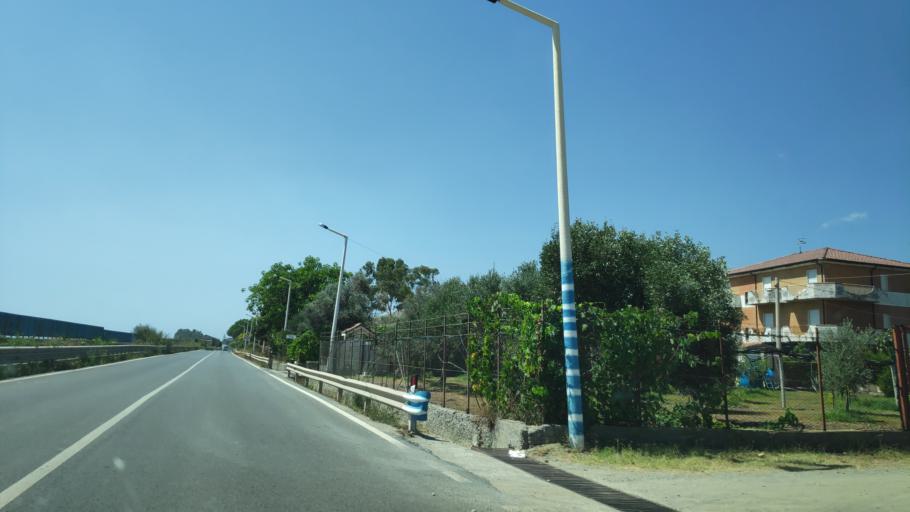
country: IT
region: Calabria
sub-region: Provincia di Reggio Calabria
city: Brancaleone-Marina
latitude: 37.9890
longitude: 16.1192
